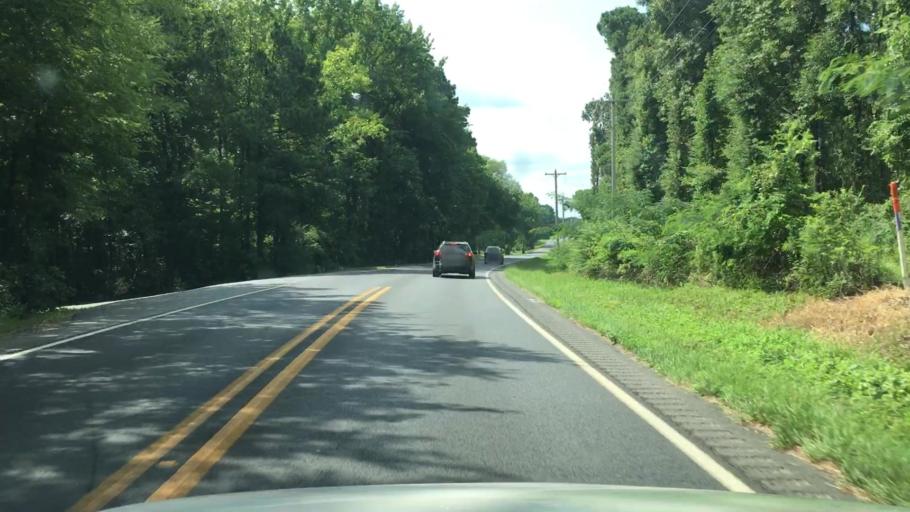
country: US
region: Arkansas
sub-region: Garland County
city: Lake Hamilton
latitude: 34.3107
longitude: -93.1685
